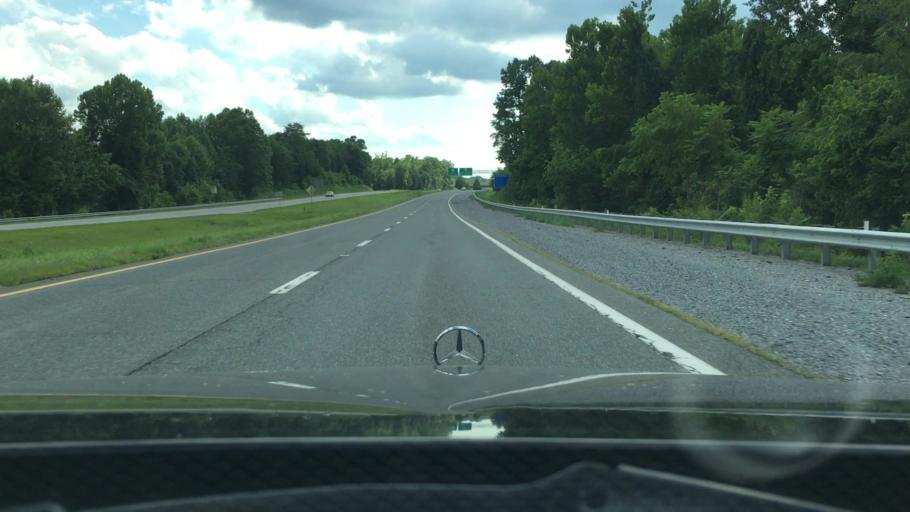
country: US
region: Virginia
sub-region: Campbell County
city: Altavista
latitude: 37.1314
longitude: -79.3000
